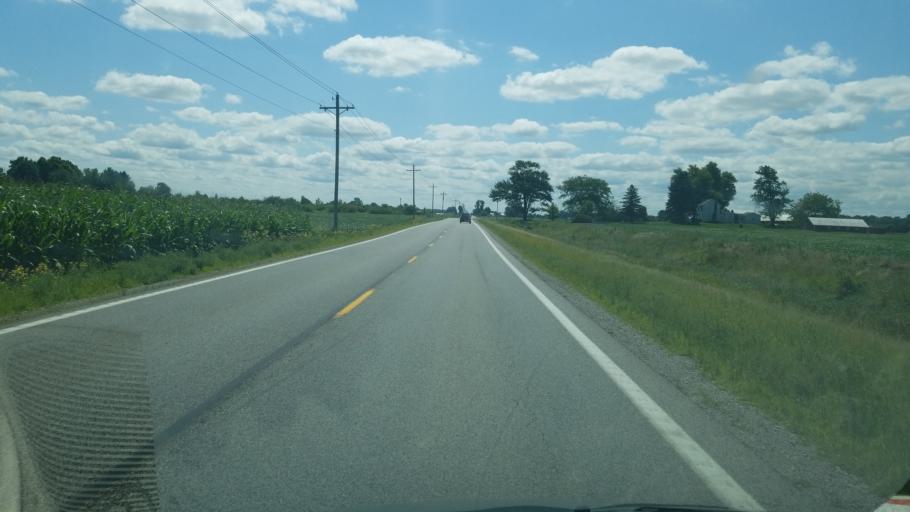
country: US
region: Ohio
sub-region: Fulton County
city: Delta
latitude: 41.6472
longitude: -84.0351
